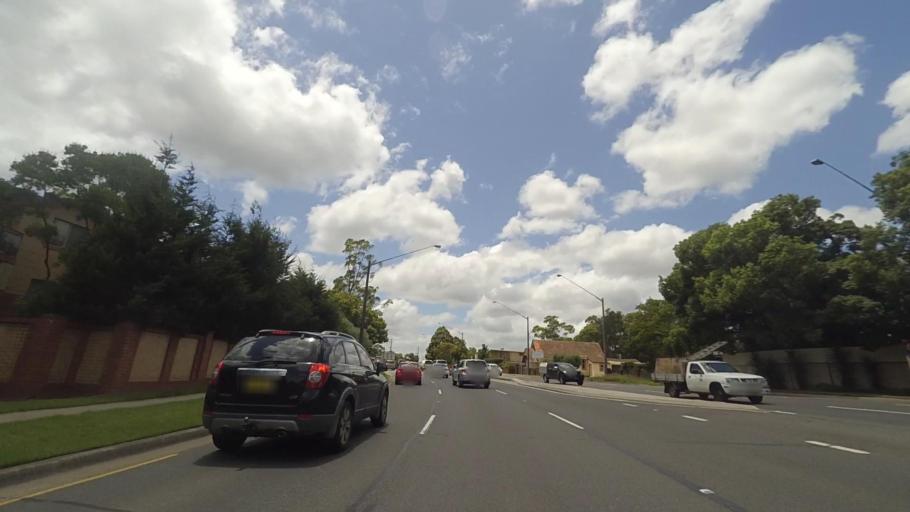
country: AU
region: New South Wales
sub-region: Hornsby Shire
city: Pennant Hills
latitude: -33.7350
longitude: 151.0764
